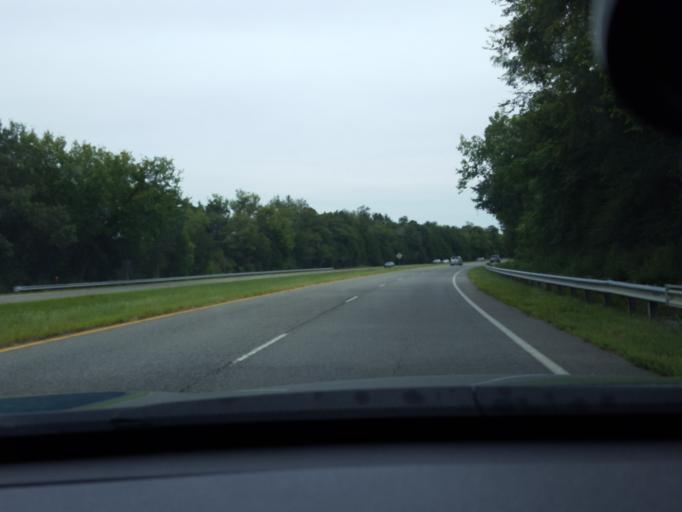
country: US
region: Virginia
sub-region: Caroline County
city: Bowling Green
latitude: 38.0497
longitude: -77.3407
